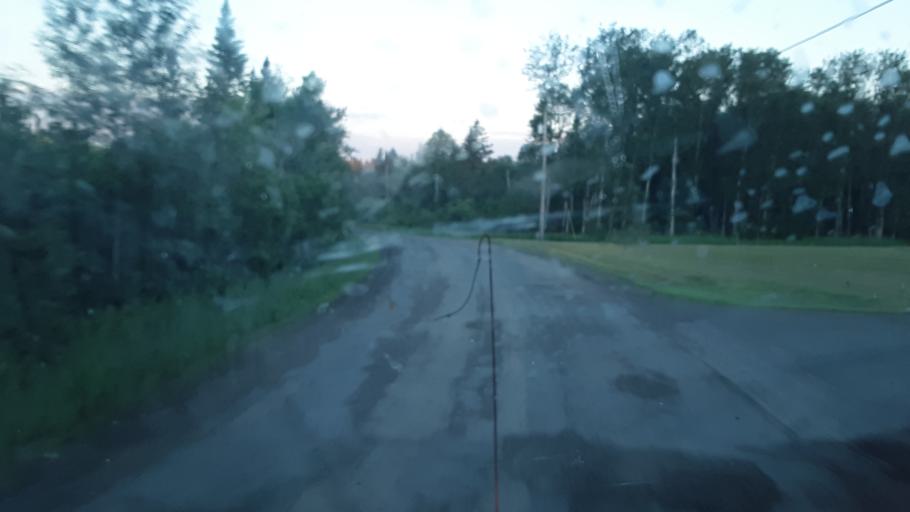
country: US
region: Maine
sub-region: Aroostook County
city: Caribou
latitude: 46.8696
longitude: -68.1324
